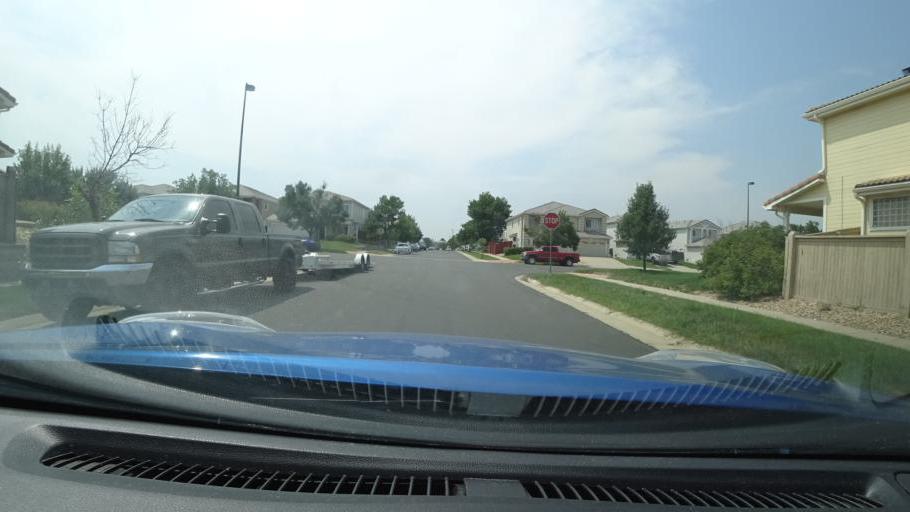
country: US
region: Colorado
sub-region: Adams County
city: Aurora
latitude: 39.7704
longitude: -104.7449
